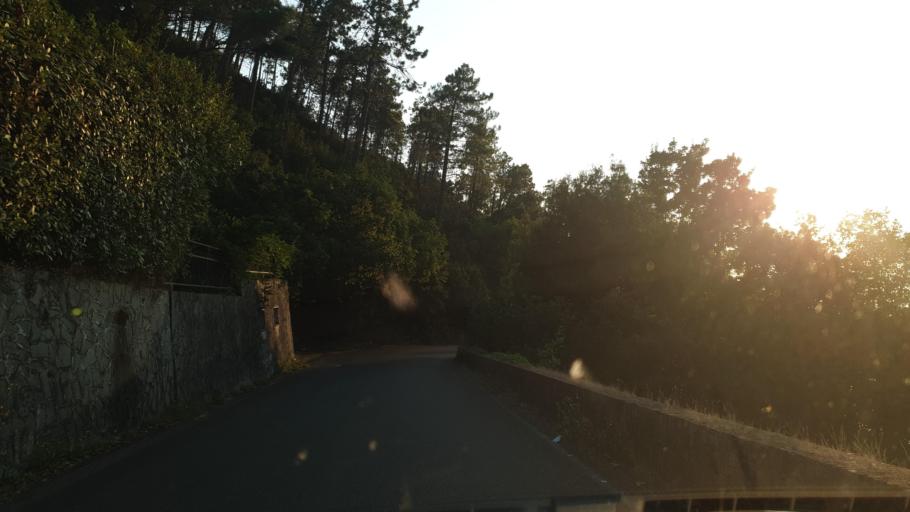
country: IT
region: Liguria
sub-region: Provincia di La Spezia
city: Bonassola
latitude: 44.1791
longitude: 9.5878
